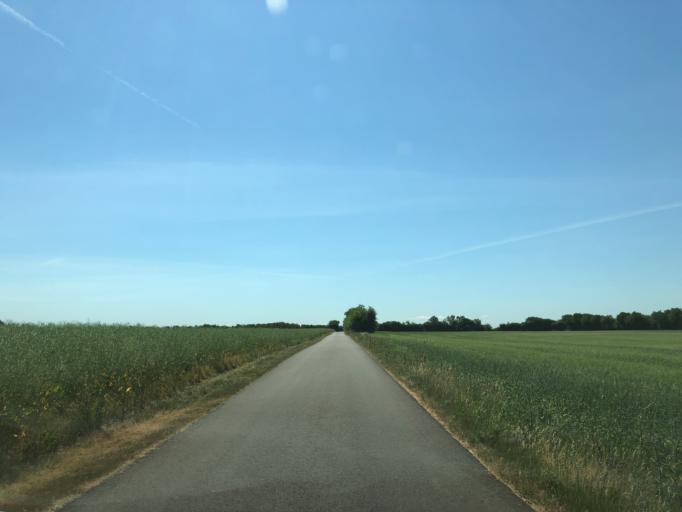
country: DK
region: Central Jutland
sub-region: Struer Kommune
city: Struer
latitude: 56.4283
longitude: 8.4391
